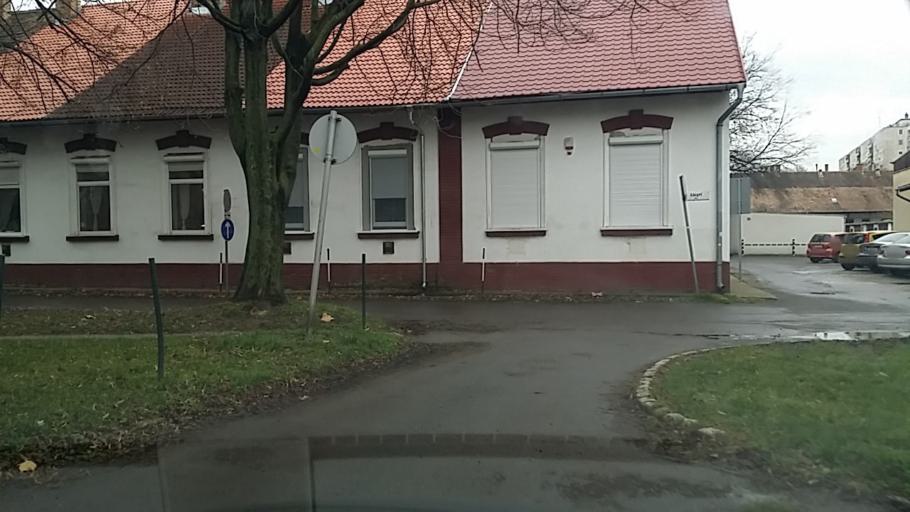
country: HU
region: Hajdu-Bihar
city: Debrecen
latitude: 47.5394
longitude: 21.6231
